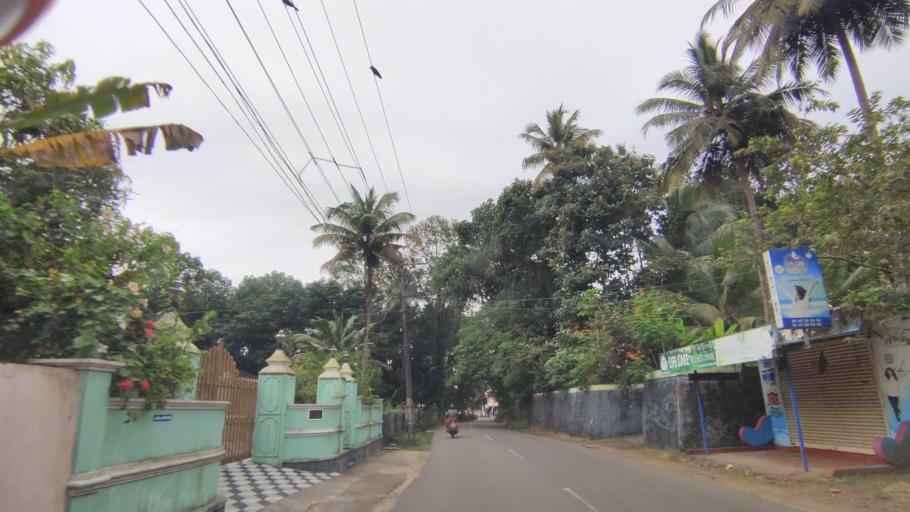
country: IN
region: Kerala
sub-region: Kottayam
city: Kottayam
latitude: 9.6775
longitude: 76.5058
